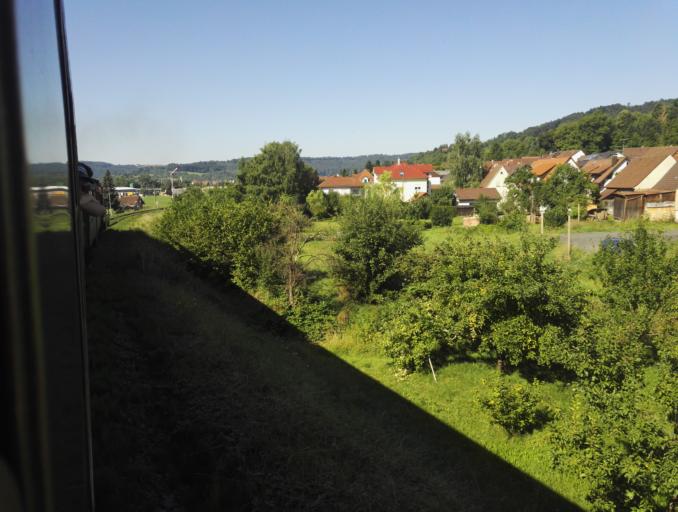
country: DE
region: Baden-Wuerttemberg
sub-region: Regierungsbezirk Stuttgart
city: Rudersberg
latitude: 48.8929
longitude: 9.5469
